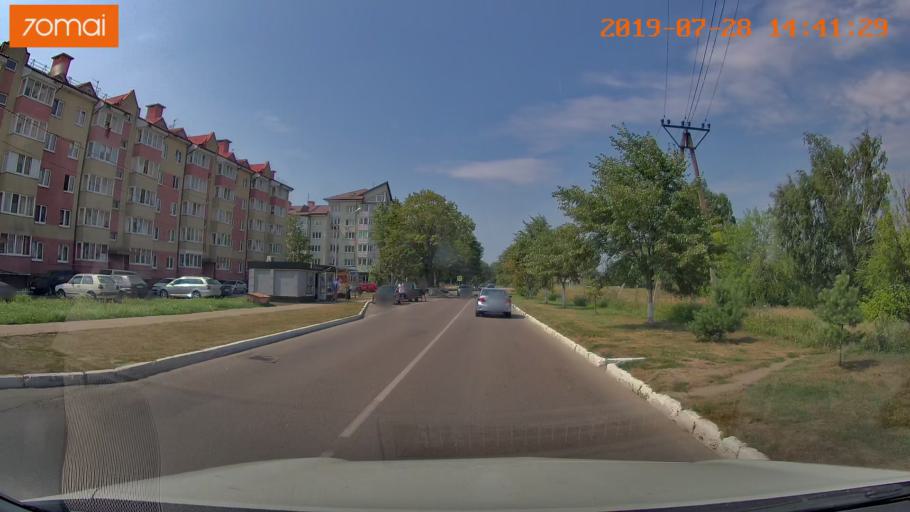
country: RU
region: Kaliningrad
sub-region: Gorod Kaliningrad
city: Yantarnyy
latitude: 54.8561
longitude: 19.9475
